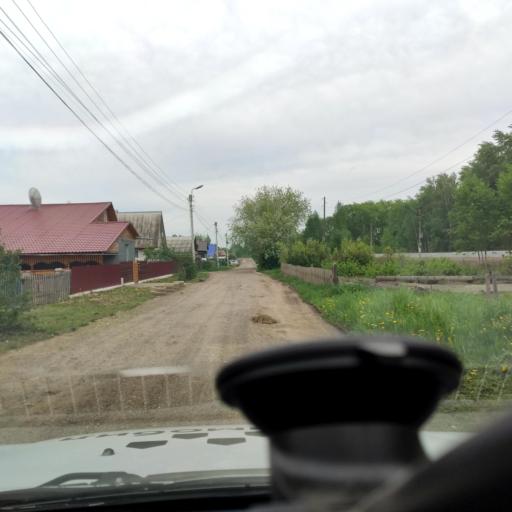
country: RU
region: Perm
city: Overyata
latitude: 58.0609
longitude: 55.8243
